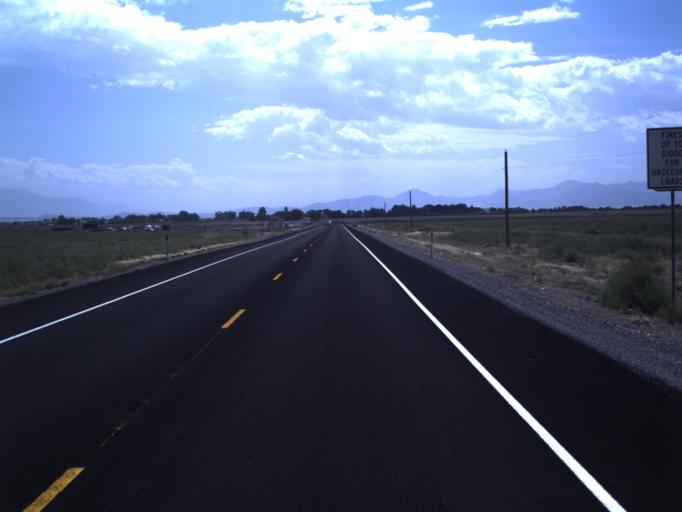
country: US
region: Utah
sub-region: Utah County
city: Eagle Mountain
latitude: 40.2799
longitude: -112.0954
